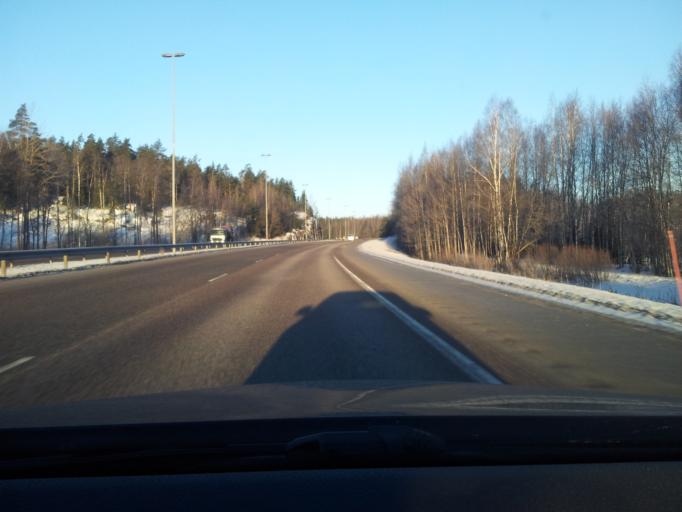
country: FI
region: Uusimaa
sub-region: Helsinki
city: Kirkkonummi
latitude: 60.2859
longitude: 24.4199
